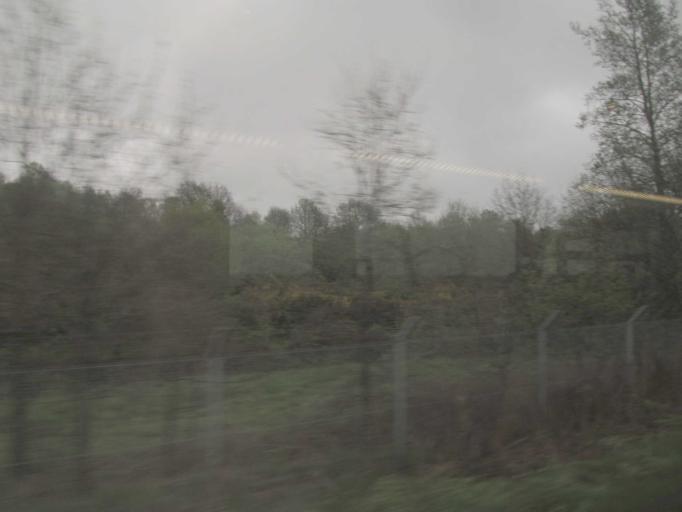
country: GB
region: England
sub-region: Surrey
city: Frimley
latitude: 51.3137
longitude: -0.7570
